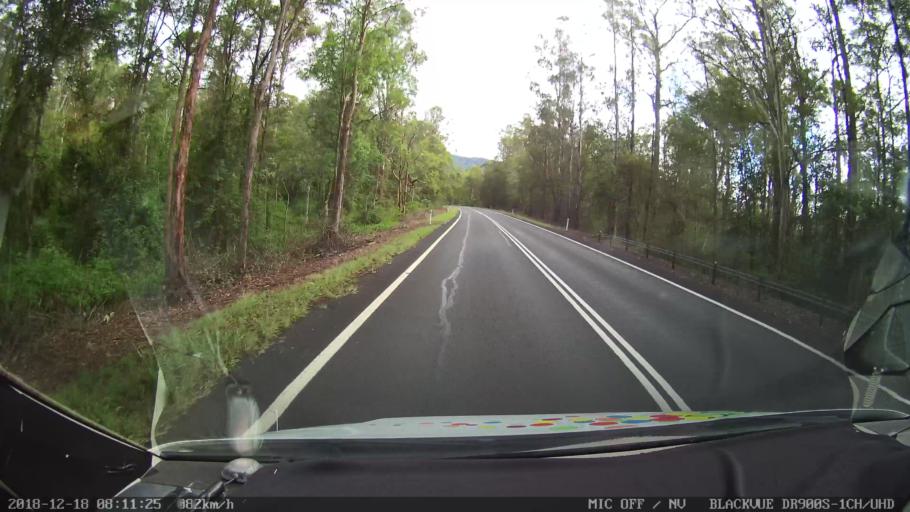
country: AU
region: New South Wales
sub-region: Kyogle
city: Kyogle
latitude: -28.3511
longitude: 152.6688
